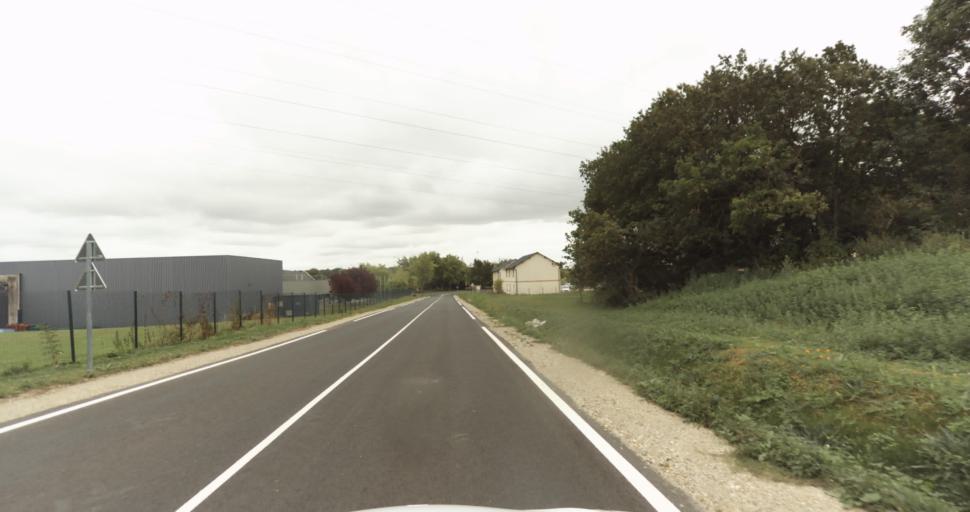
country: FR
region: Haute-Normandie
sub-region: Departement de l'Eure
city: Gravigny
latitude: 49.0341
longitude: 1.1807
